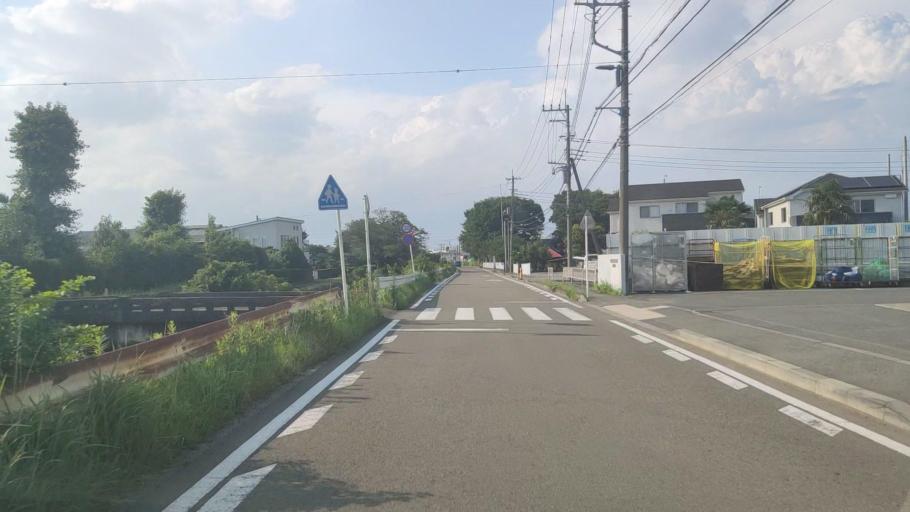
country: JP
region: Kanagawa
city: Isehara
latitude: 35.3881
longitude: 139.3385
